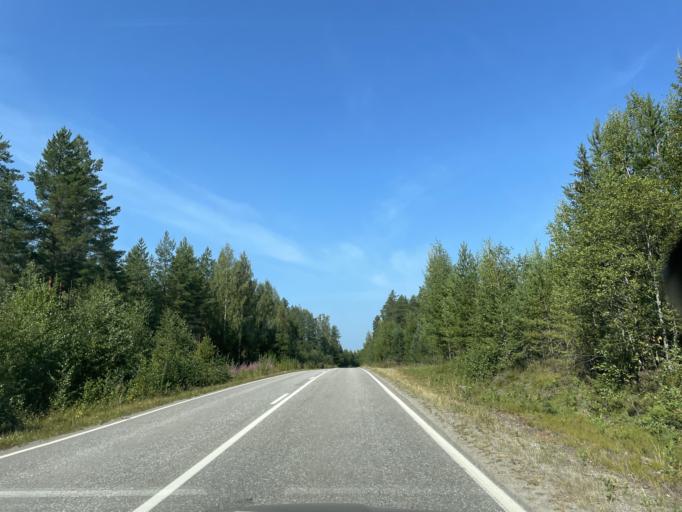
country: FI
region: Central Finland
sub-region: Saarijaervi-Viitasaari
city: Pihtipudas
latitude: 63.3695
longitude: 25.6213
